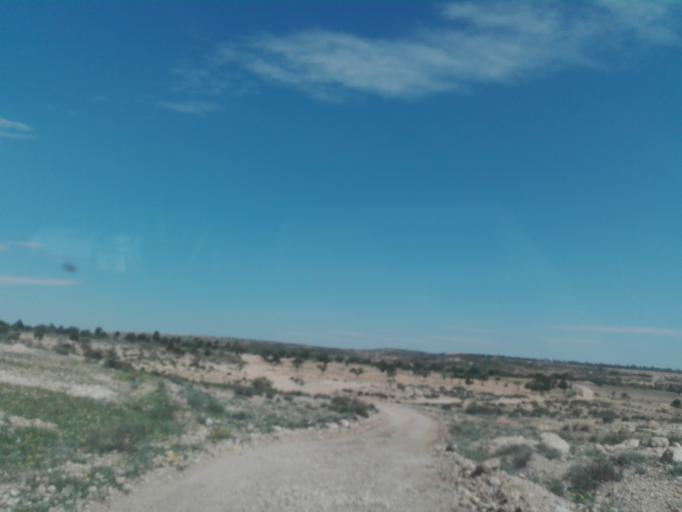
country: TN
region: Safaqis
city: Sfax
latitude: 34.6900
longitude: 10.5304
